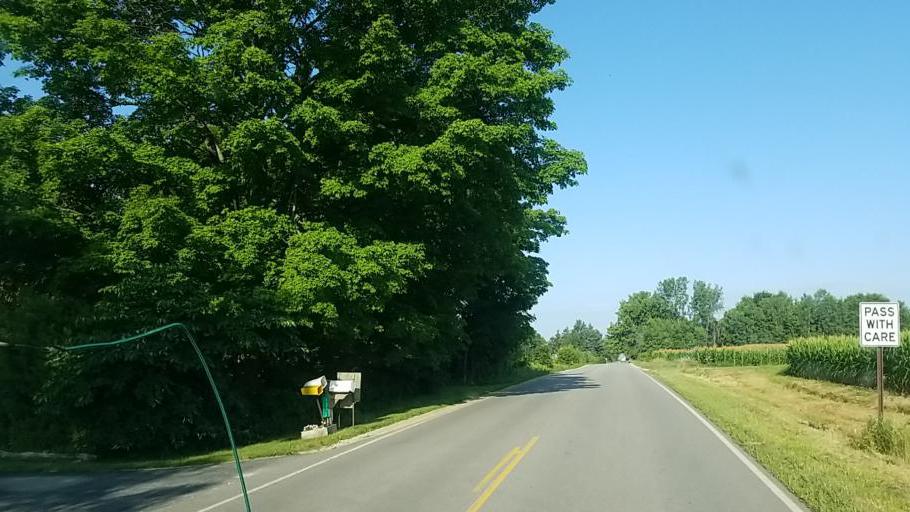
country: US
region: Michigan
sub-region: Newaygo County
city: Newaygo
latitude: 43.3511
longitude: -85.8347
